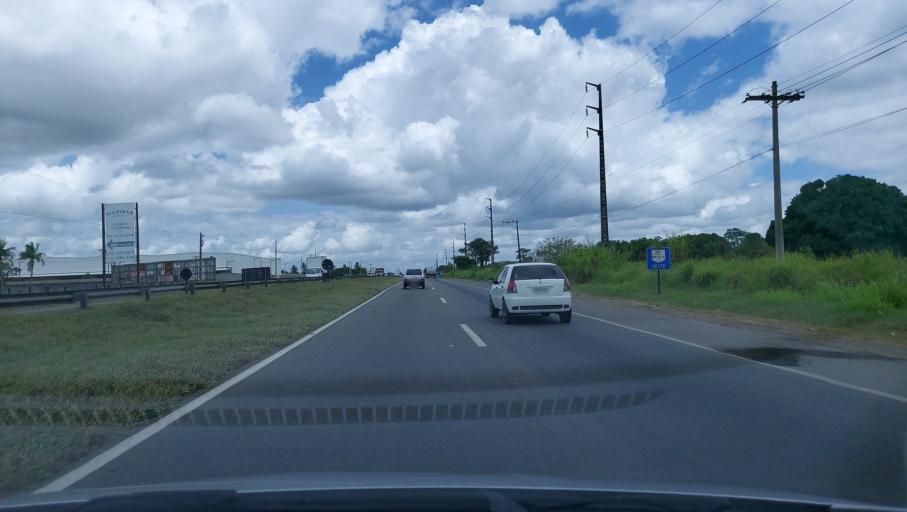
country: BR
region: Bahia
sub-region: Conceicao Do Jacuipe
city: Conceicao do Jacuipe
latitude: -12.3754
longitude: -38.8053
